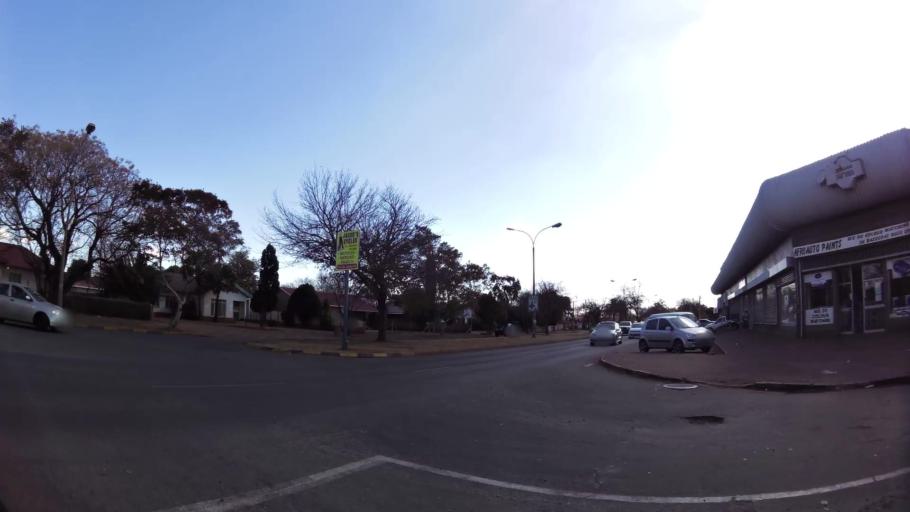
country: ZA
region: Gauteng
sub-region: West Rand District Municipality
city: Carletonville
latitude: -26.3551
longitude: 27.3946
